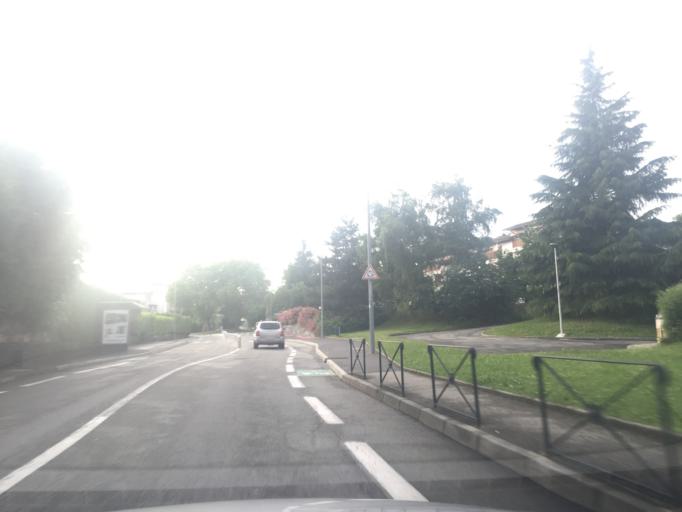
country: FR
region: Rhone-Alpes
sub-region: Departement de la Savoie
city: Bassens
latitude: 45.5872
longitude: 5.9223
